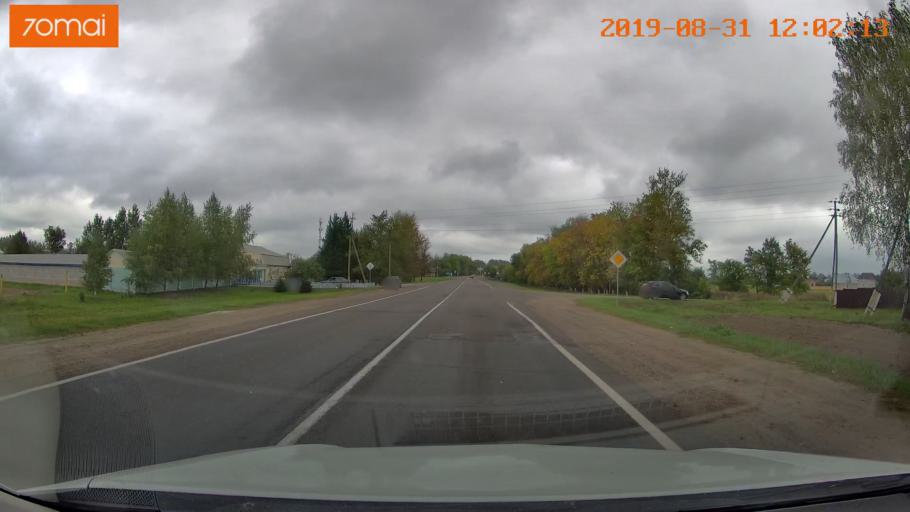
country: BY
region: Mogilev
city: Horad Krychaw
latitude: 53.6948
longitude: 31.6941
